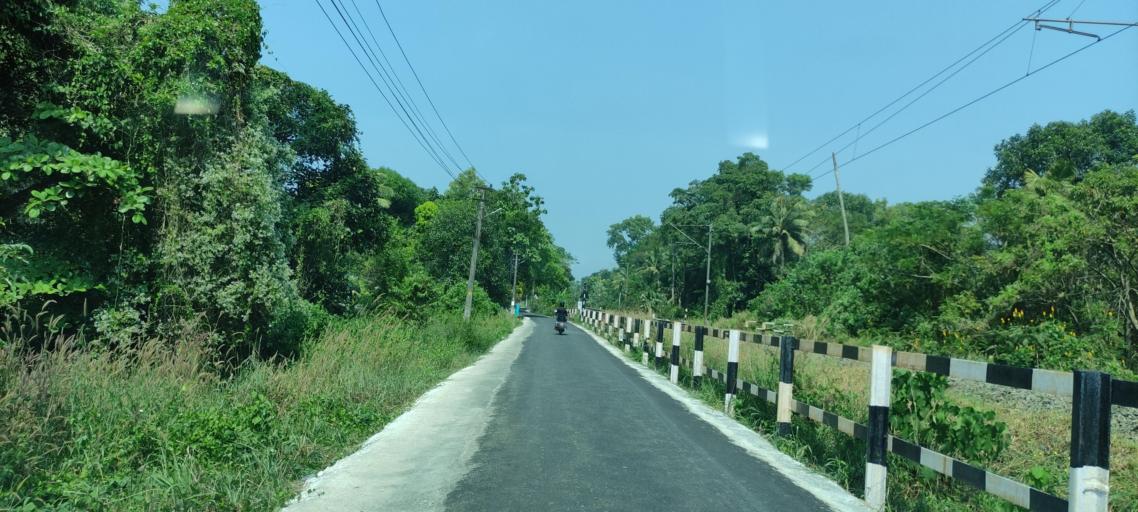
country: IN
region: Kerala
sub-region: Alappuzha
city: Alleppey
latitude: 9.5356
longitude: 76.3210
